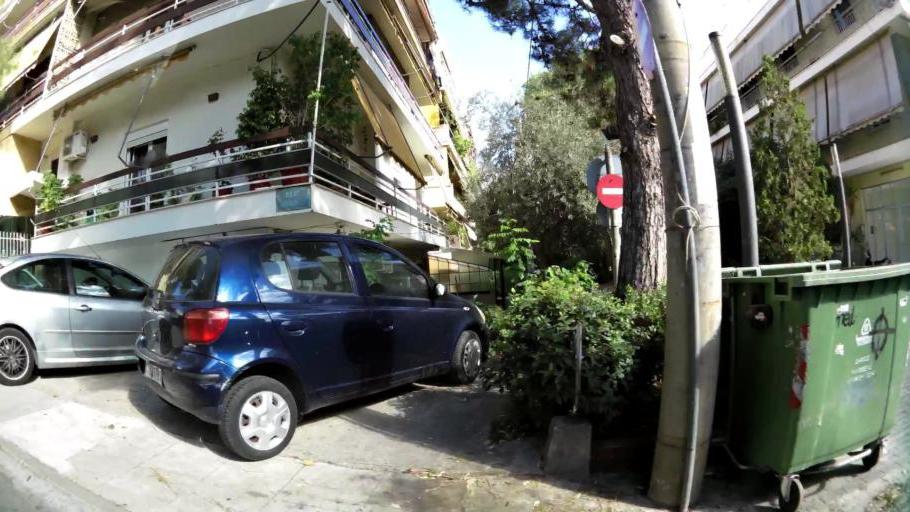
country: GR
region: Attica
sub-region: Nomarchia Athinas
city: Neo Psychiko
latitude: 38.0041
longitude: 23.7834
